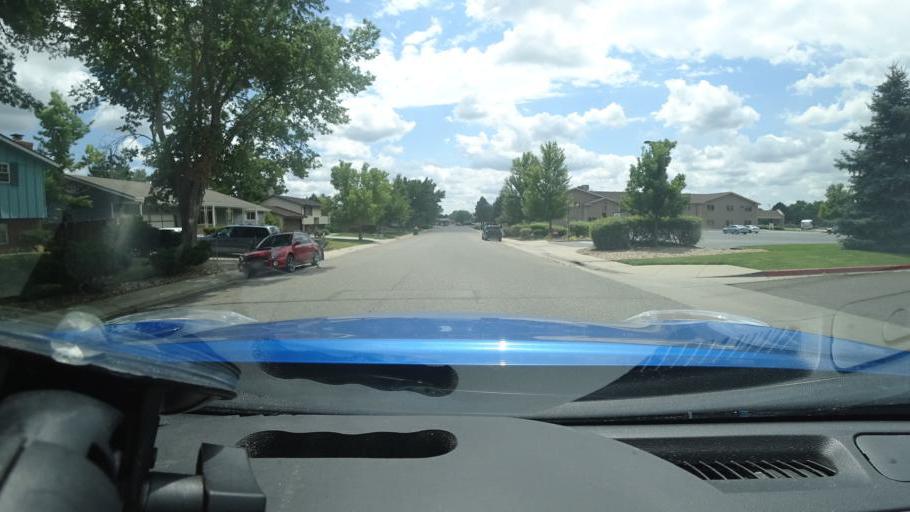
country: US
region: Colorado
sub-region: Adams County
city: Aurora
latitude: 39.6984
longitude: -104.8351
